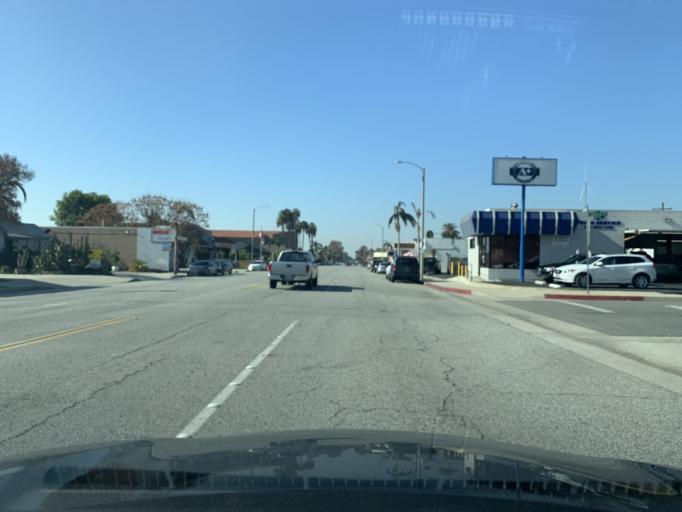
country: US
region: California
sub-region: Los Angeles County
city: Covina
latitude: 34.0907
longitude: -117.8840
